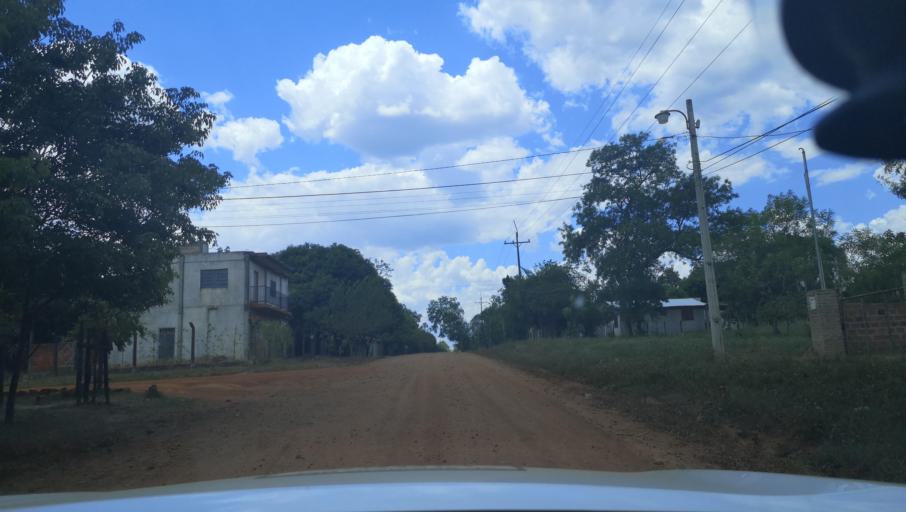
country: PY
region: Itapua
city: Carmen del Parana
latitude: -27.1711
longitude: -56.2428
